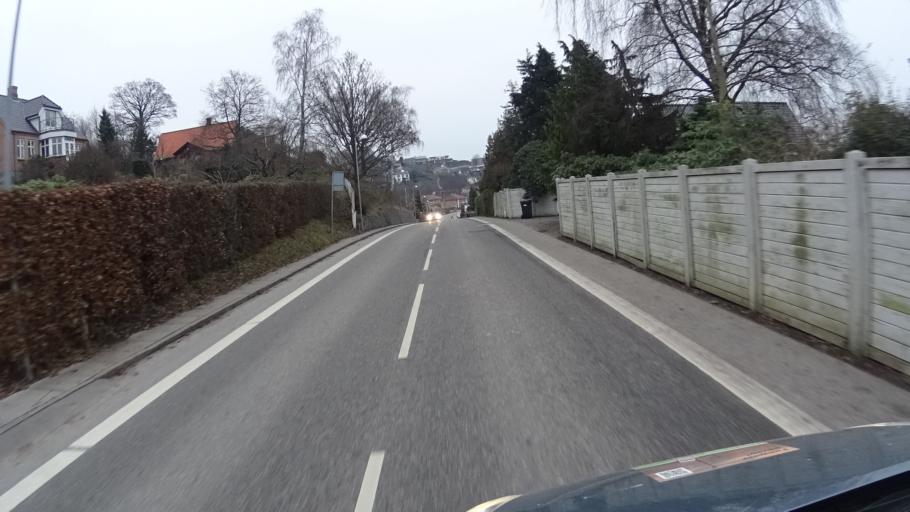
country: DK
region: South Denmark
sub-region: Vejle Kommune
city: Vejle
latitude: 55.7072
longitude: 9.5942
